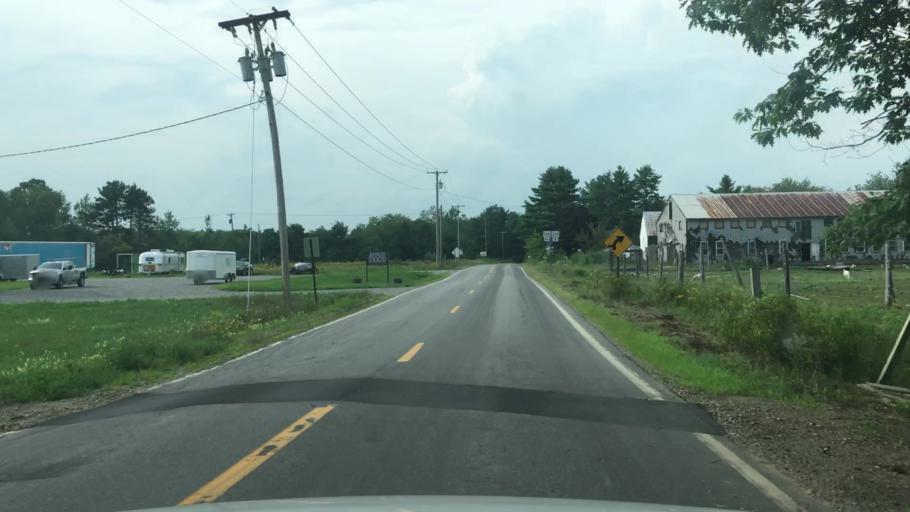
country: US
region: Maine
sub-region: Knox County
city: Washington
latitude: 44.2259
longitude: -69.3877
